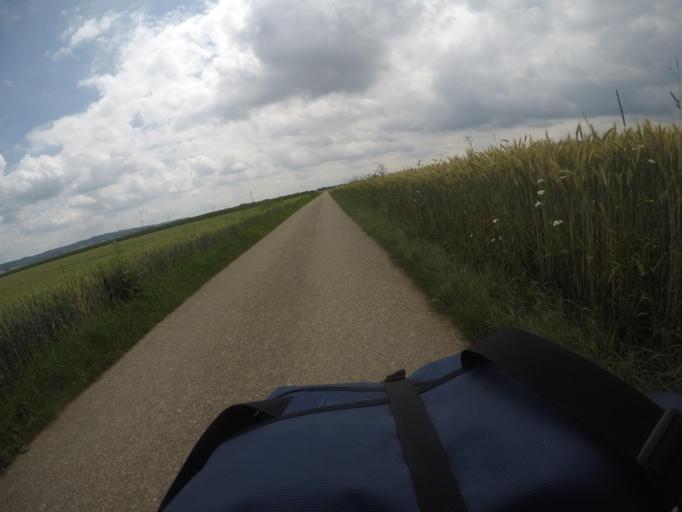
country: DE
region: Bavaria
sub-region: Swabia
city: Heimertingen
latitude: 48.0570
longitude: 10.1561
